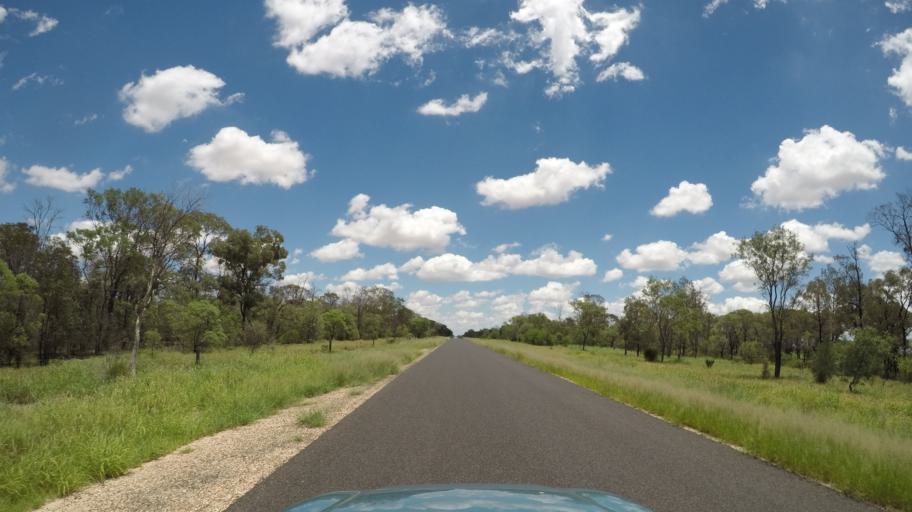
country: AU
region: Queensland
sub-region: Goondiwindi
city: Goondiwindi
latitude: -28.1678
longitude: 150.1919
